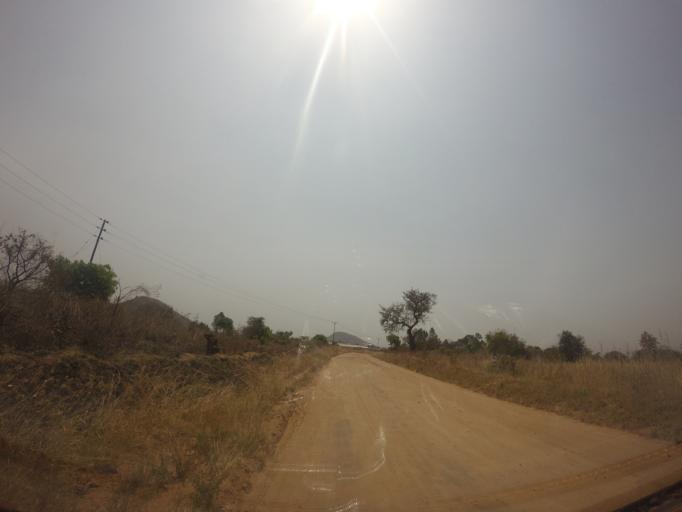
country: UG
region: Northern Region
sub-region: Arua District
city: Arua
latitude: 2.9401
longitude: 30.9809
